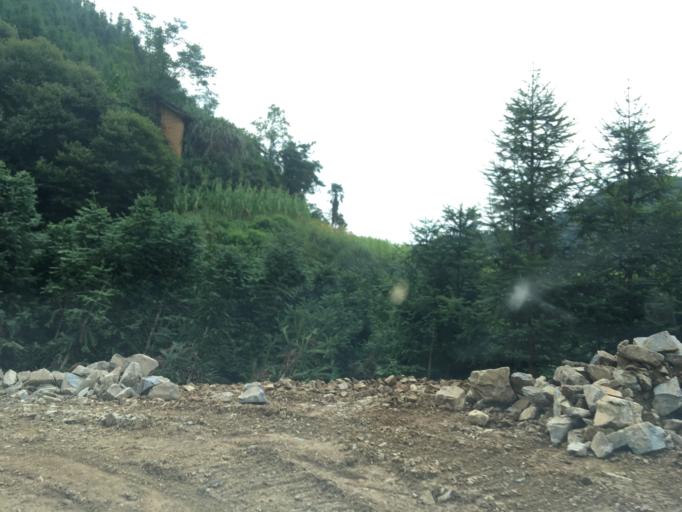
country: CN
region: Guangxi Zhuangzu Zizhiqu
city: Xinzhou
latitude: 24.8686
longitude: 105.8665
